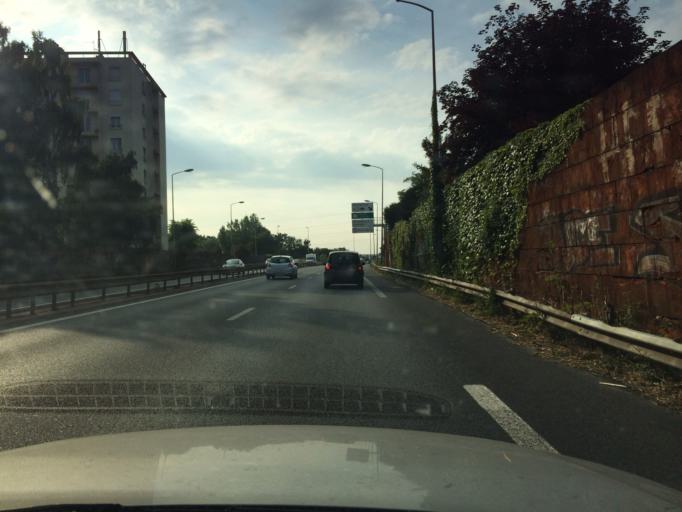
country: FR
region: Lower Normandy
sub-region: Departement du Calvados
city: Mondeville
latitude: 49.1788
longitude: -0.3207
